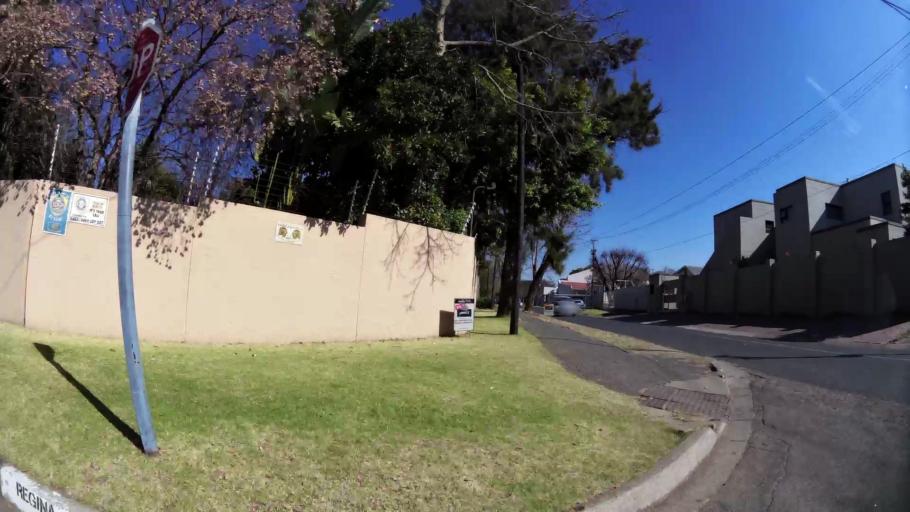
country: ZA
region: Gauteng
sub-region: City of Johannesburg Metropolitan Municipality
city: Modderfontein
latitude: -26.1423
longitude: 28.1049
